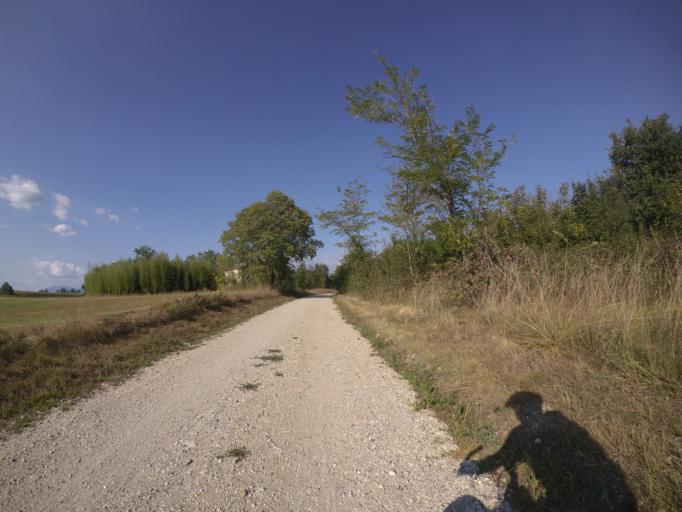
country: IT
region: Friuli Venezia Giulia
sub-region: Provincia di Udine
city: Zugliano-Terenzano-Cargnacco
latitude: 46.0121
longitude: 13.1904
